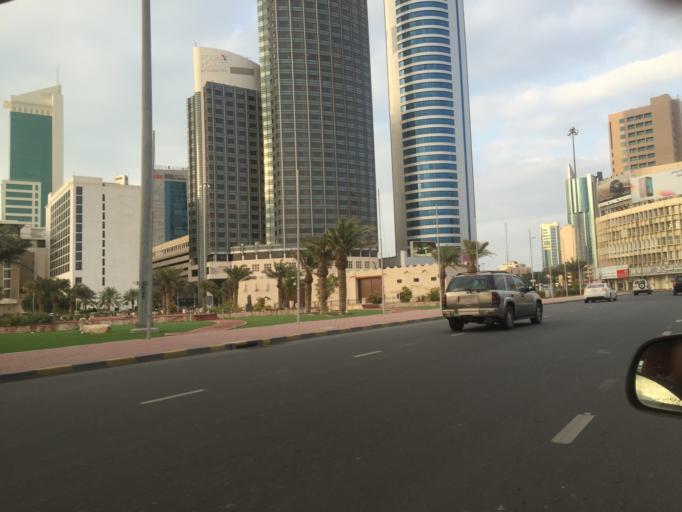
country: KW
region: Al Asimah
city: Ash Shamiyah
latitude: 29.3599
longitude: 47.9638
